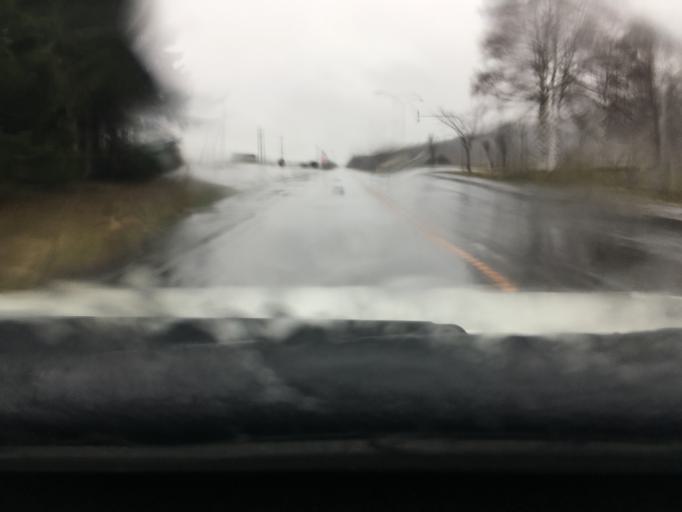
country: JP
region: Hokkaido
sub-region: Asahikawa-shi
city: Asahikawa
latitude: 43.9388
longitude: 142.4649
